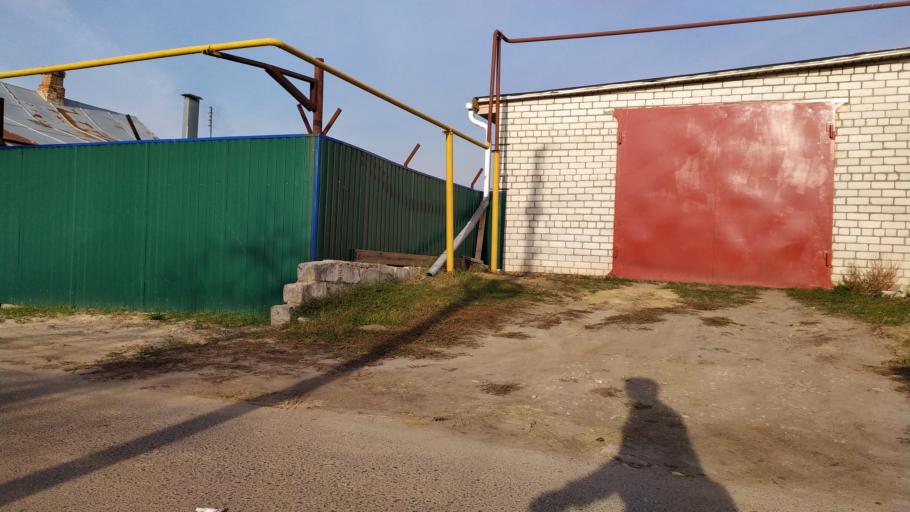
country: RU
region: Kursk
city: Kursk
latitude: 51.6444
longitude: 36.1467
